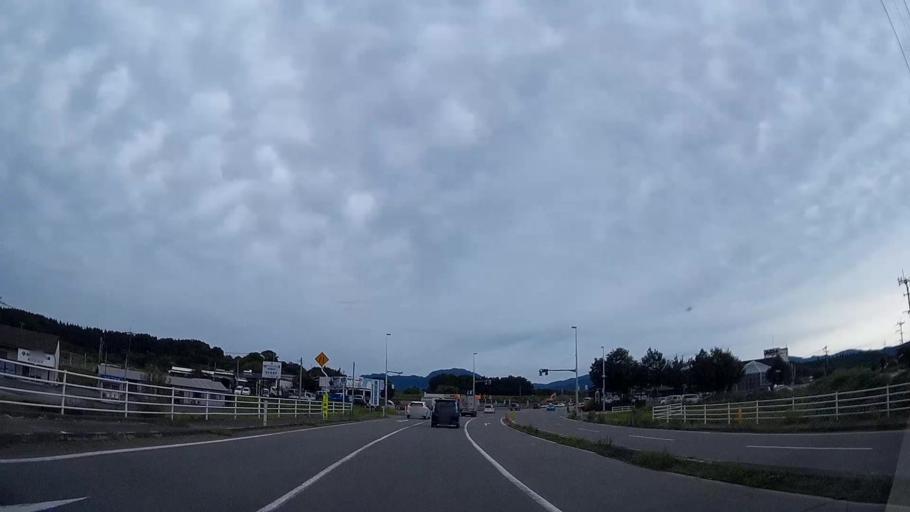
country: JP
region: Kumamoto
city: Kikuchi
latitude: 32.9461
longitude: 130.8225
